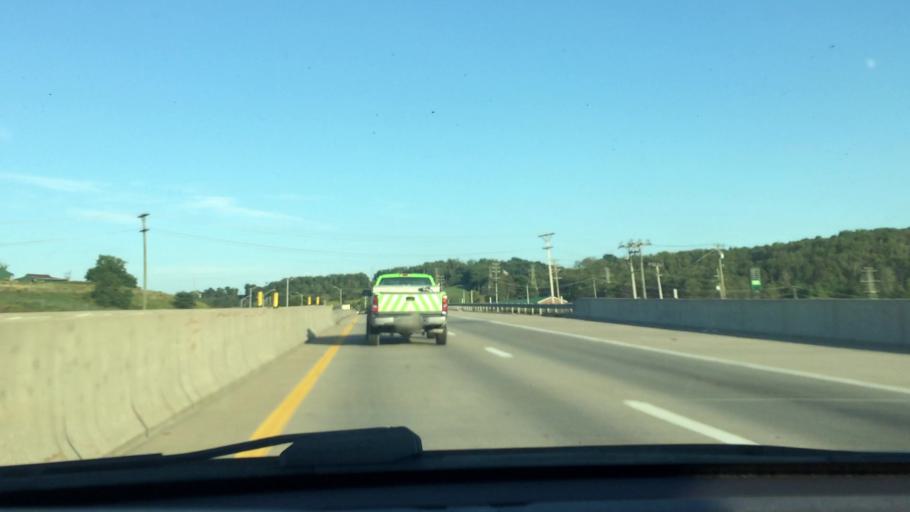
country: US
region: Pennsylvania
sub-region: Washington County
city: East Washington
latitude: 40.1571
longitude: -80.1285
